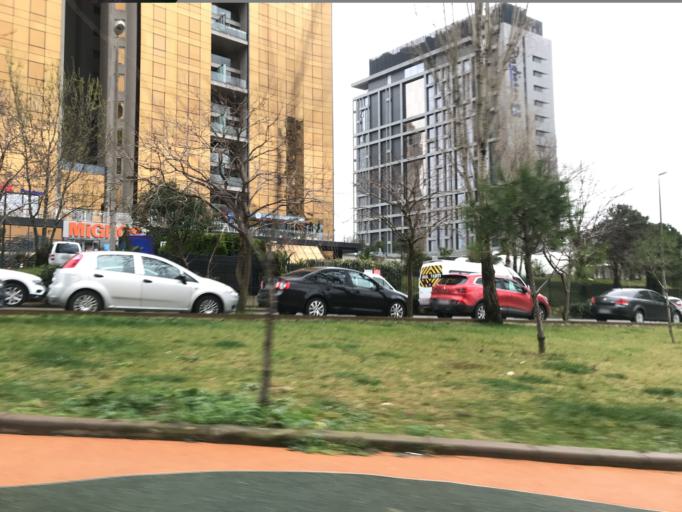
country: TR
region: Istanbul
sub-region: Atasehir
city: Atasehir
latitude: 40.9920
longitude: 29.1169
